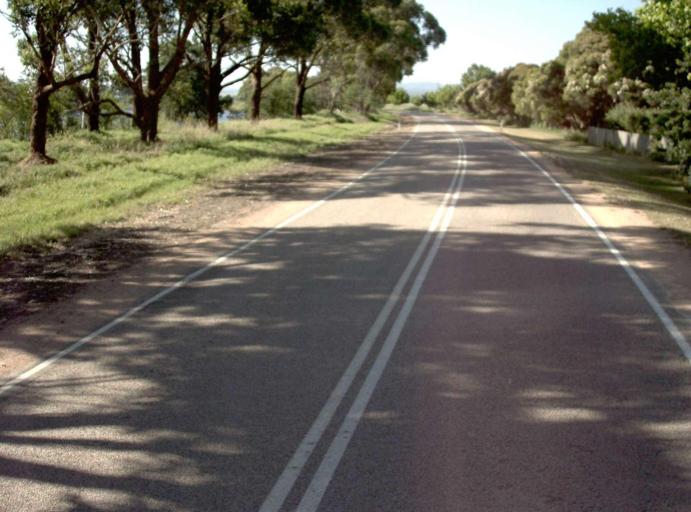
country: AU
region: Victoria
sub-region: East Gippsland
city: Lakes Entrance
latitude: -37.7631
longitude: 148.5389
